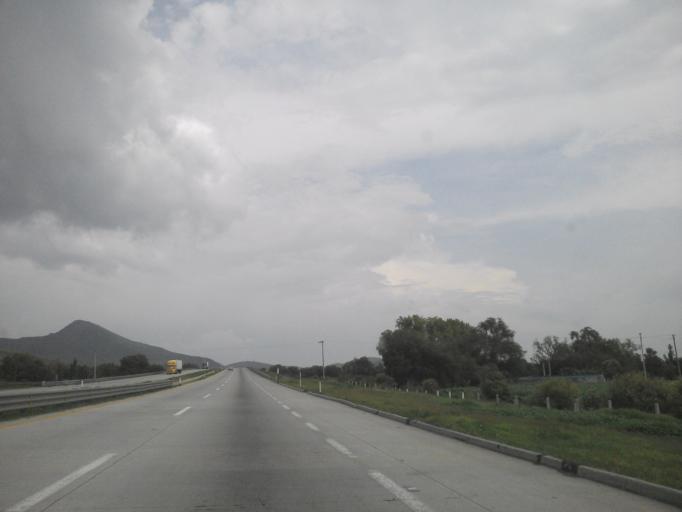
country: MX
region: Hidalgo
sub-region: Atitalaquia
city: Tezoquipa
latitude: 20.0549
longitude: -99.1919
